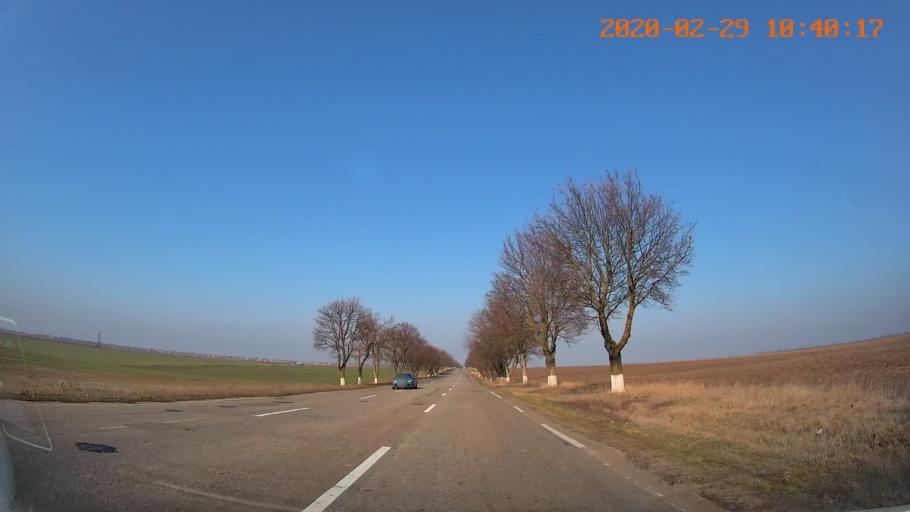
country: MD
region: Anenii Noi
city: Varnita
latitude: 47.0316
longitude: 29.4419
